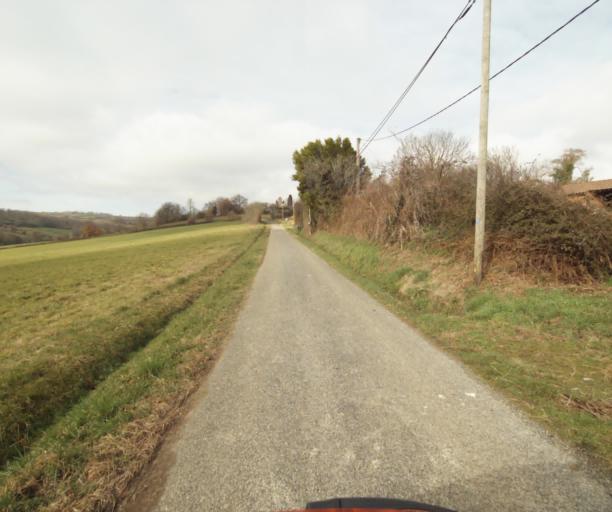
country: FR
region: Midi-Pyrenees
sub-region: Departement de l'Ariege
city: Pamiers
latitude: 43.1045
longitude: 1.5204
